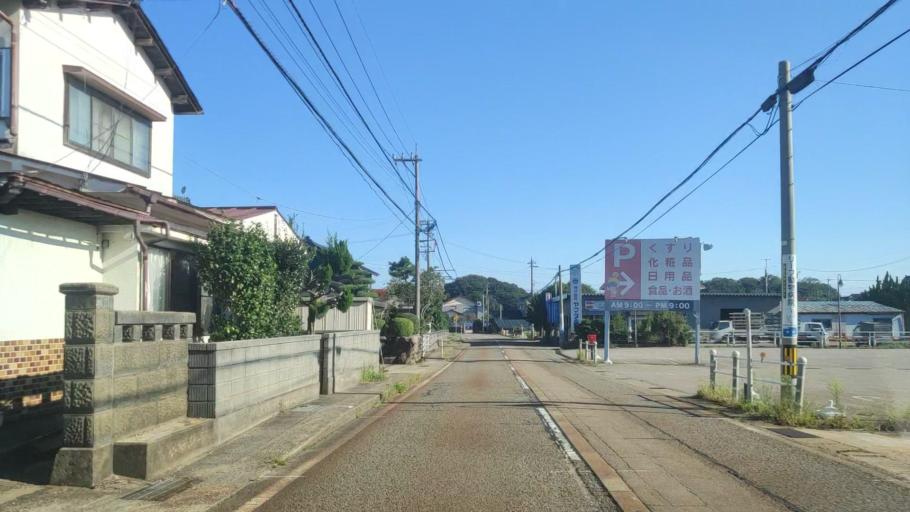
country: JP
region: Ishikawa
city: Hakui
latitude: 36.8269
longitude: 136.7583
